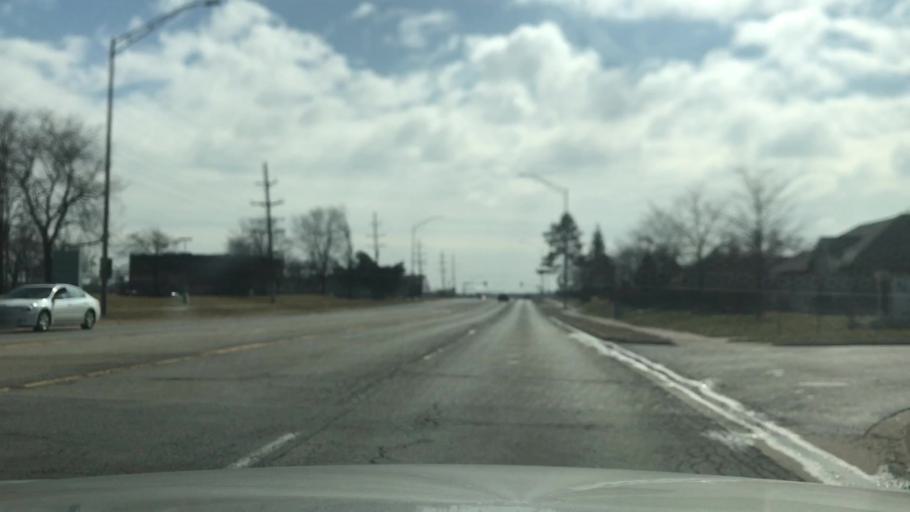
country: US
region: Illinois
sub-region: DuPage County
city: Darien
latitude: 41.7398
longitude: -87.9735
